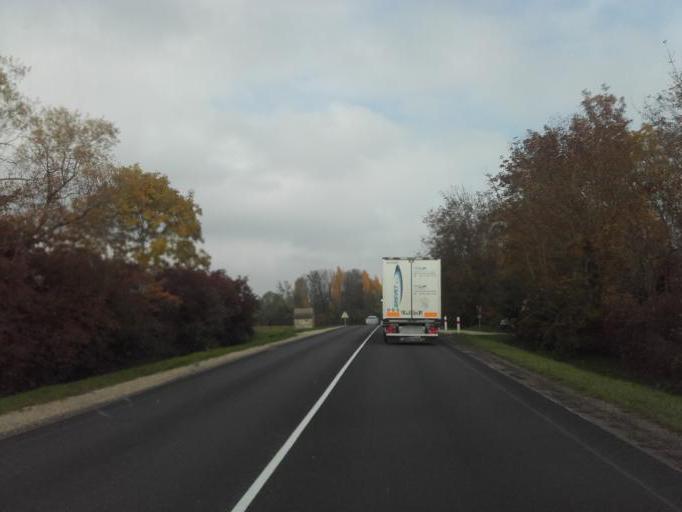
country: FR
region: Bourgogne
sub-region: Departement de la Cote-d'Or
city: Meursault
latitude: 46.9612
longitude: 4.7697
